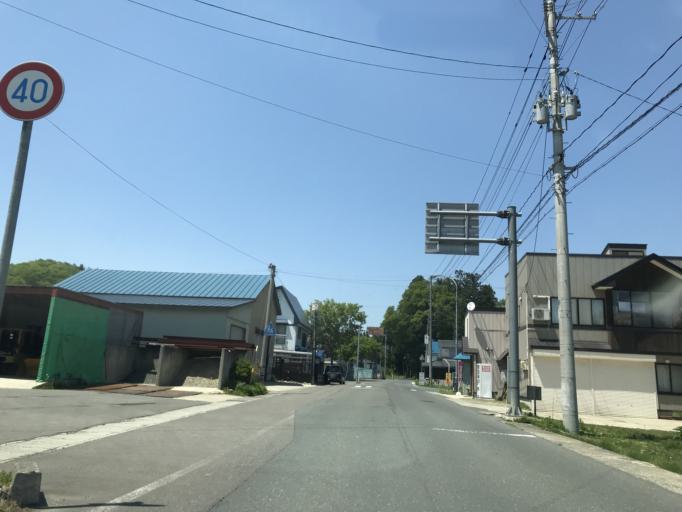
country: JP
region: Akita
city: Yokotemachi
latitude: 39.3536
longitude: 140.7685
